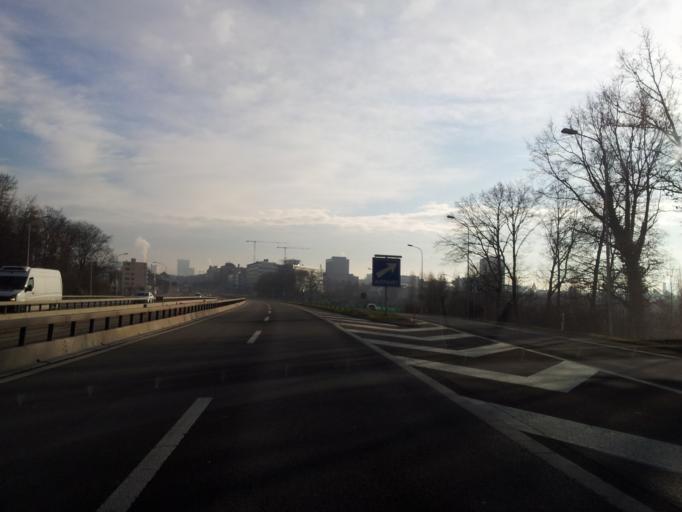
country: CH
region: Zurich
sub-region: Bezirk Zuerich
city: Zuerich (Kreis 9) / Altstetten
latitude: 47.3976
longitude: 8.4773
